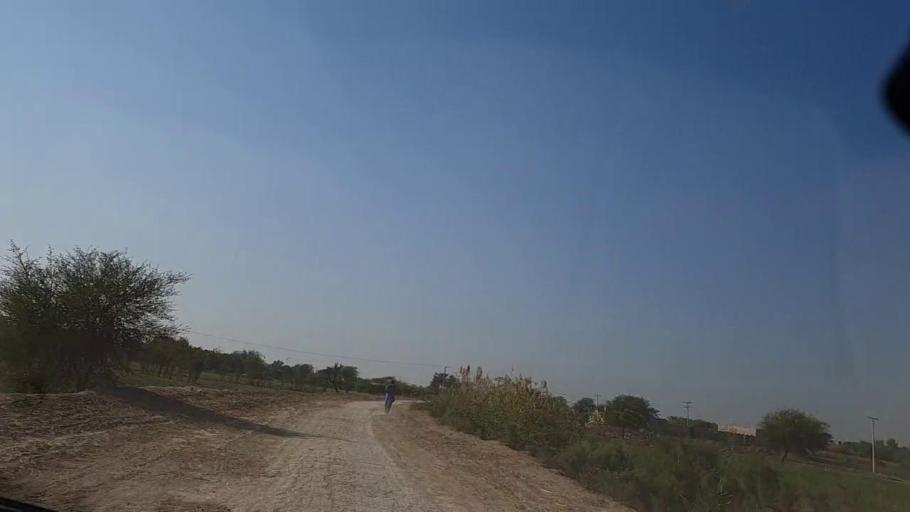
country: PK
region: Sindh
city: Mirpur Khas
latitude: 25.5195
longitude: 68.9277
